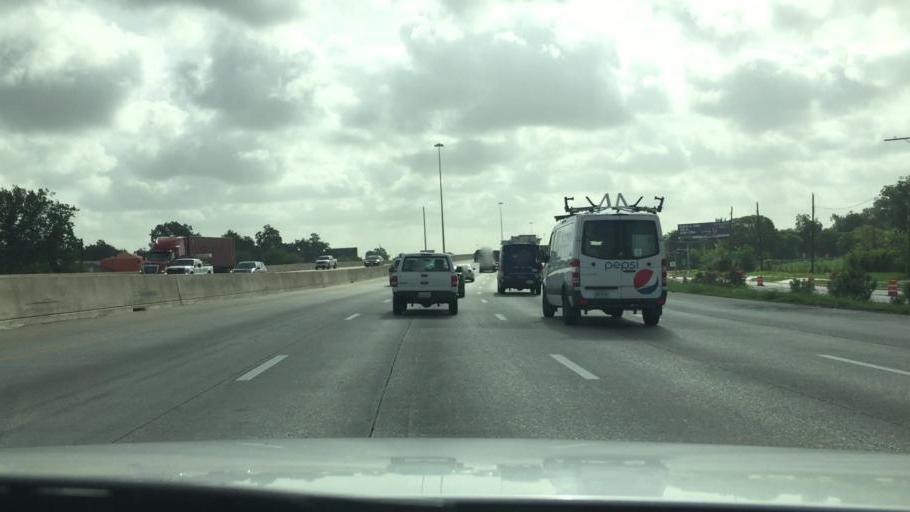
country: US
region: Texas
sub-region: Harris County
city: Houston
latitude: 29.8134
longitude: -95.3939
